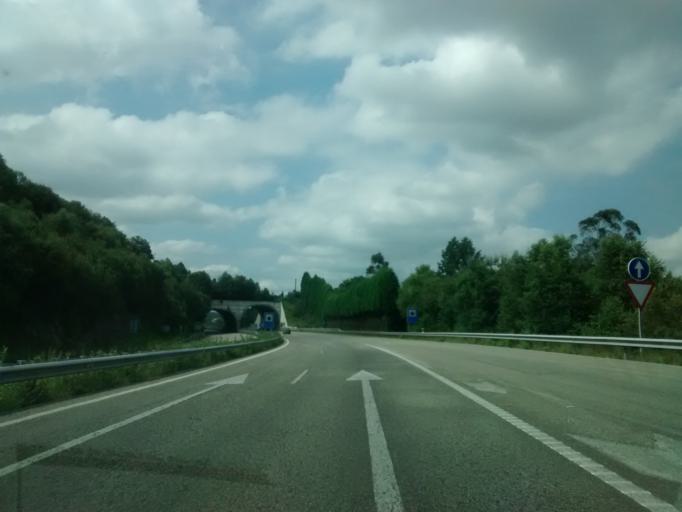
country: ES
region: Asturias
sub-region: Province of Asturias
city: Pola de Siero
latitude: 43.3572
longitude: -5.6812
